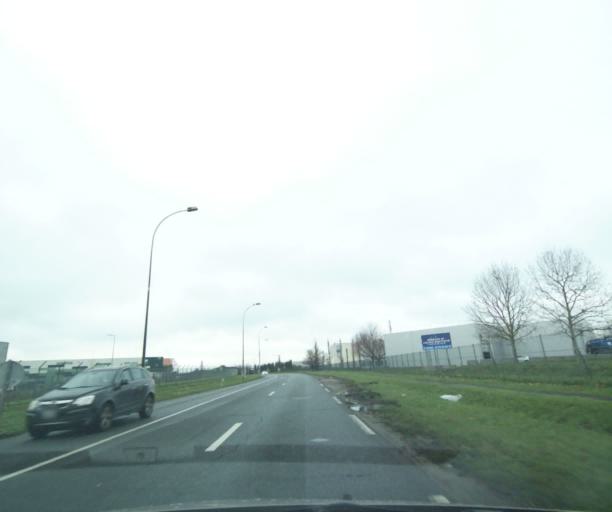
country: FR
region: Ile-de-France
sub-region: Departement du Val-de-Marne
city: Villeneuve-le-Roi
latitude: 48.7226
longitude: 2.4057
